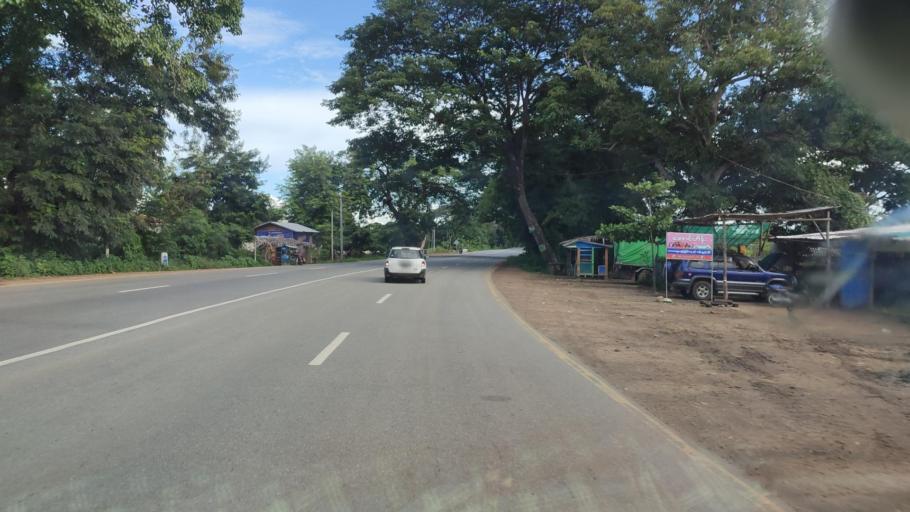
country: MM
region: Mandalay
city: Yamethin
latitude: 20.2189
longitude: 96.1815
